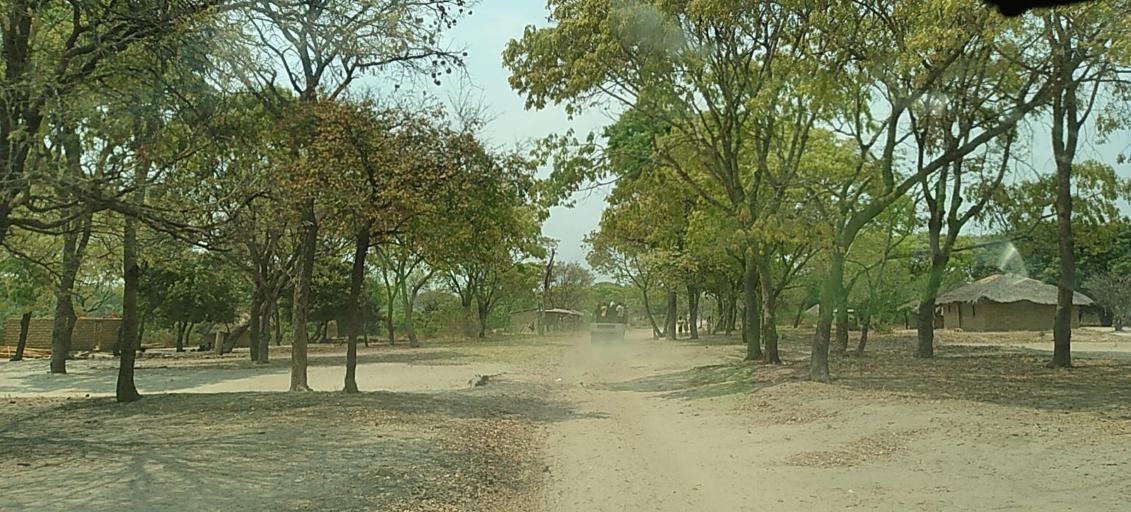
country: ZM
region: North-Western
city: Kabompo
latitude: -13.4913
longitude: 24.4635
